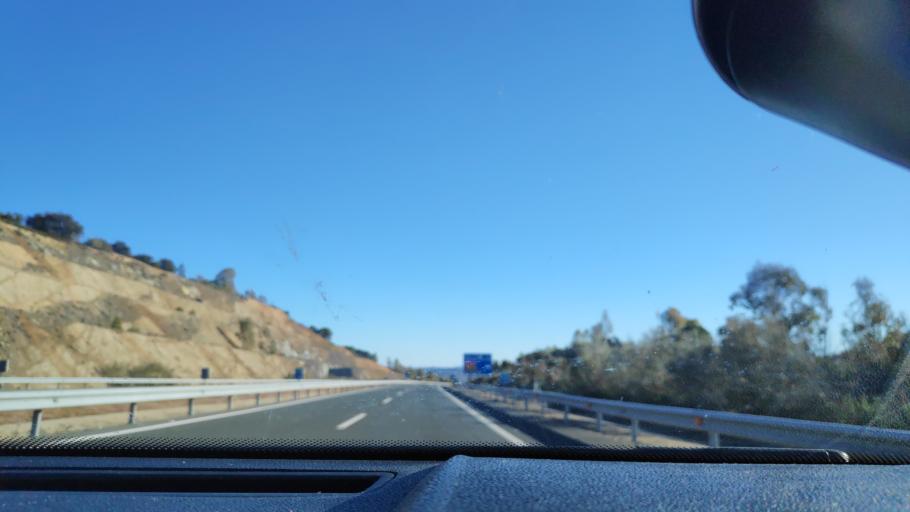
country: ES
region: Extremadura
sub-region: Provincia de Badajoz
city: Monesterio
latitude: 38.0403
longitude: -6.2278
